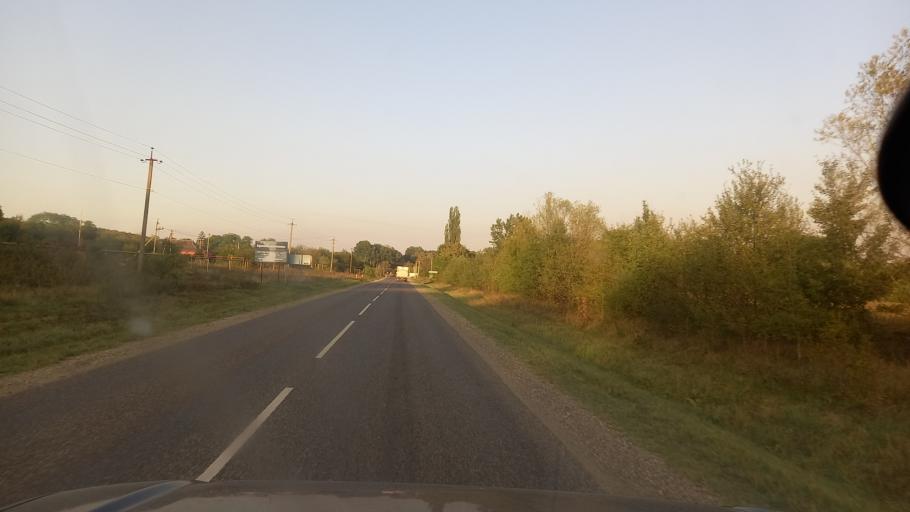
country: RU
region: Krasnodarskiy
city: Smolenskaya
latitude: 44.7631
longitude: 38.7727
